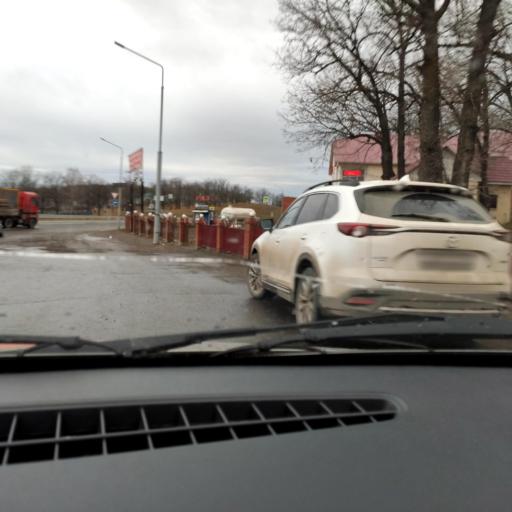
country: RU
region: Bashkortostan
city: Avdon
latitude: 54.6399
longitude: 55.5918
